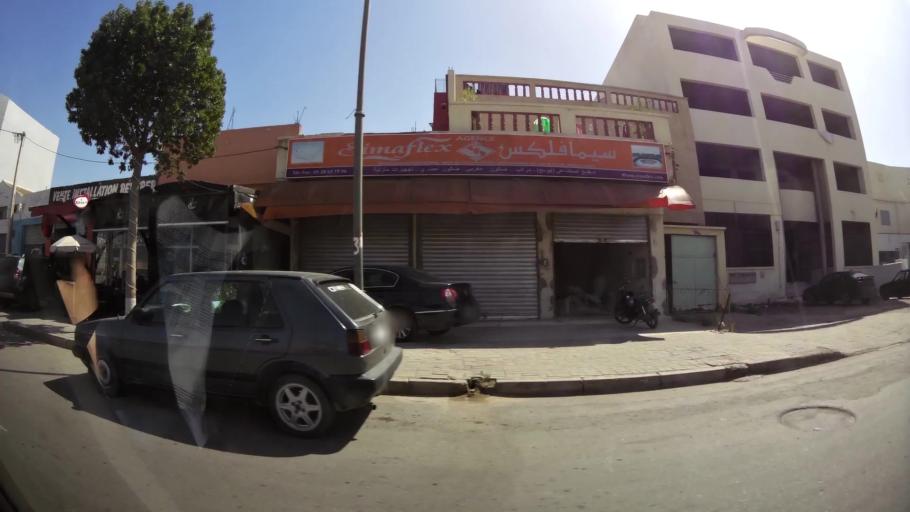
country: MA
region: Souss-Massa-Draa
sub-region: Inezgane-Ait Mellou
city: Inezgane
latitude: 30.3632
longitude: -9.5361
